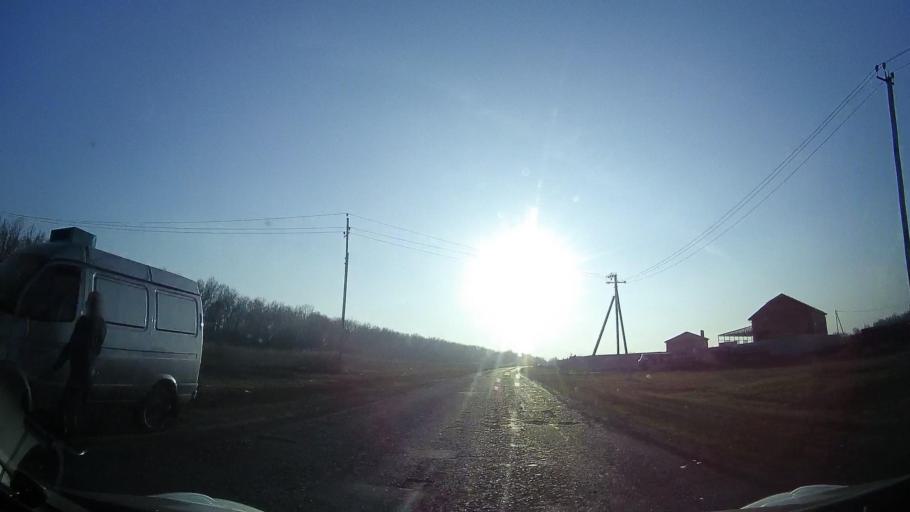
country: RU
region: Rostov
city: Ol'ginskaya
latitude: 47.1369
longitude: 39.8946
